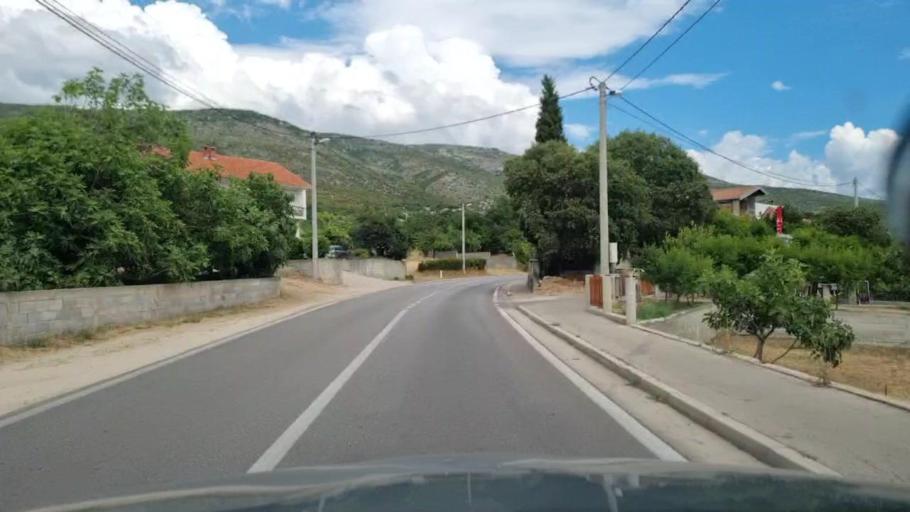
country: BA
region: Federation of Bosnia and Herzegovina
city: Blagaj
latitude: 43.2816
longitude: 17.8672
